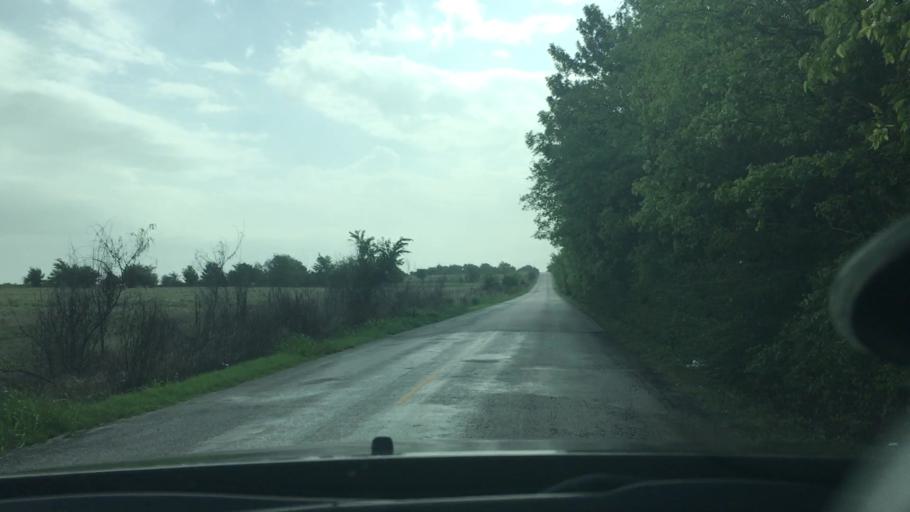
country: US
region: Oklahoma
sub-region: Carter County
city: Lone Grove
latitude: 34.2020
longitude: -97.2246
